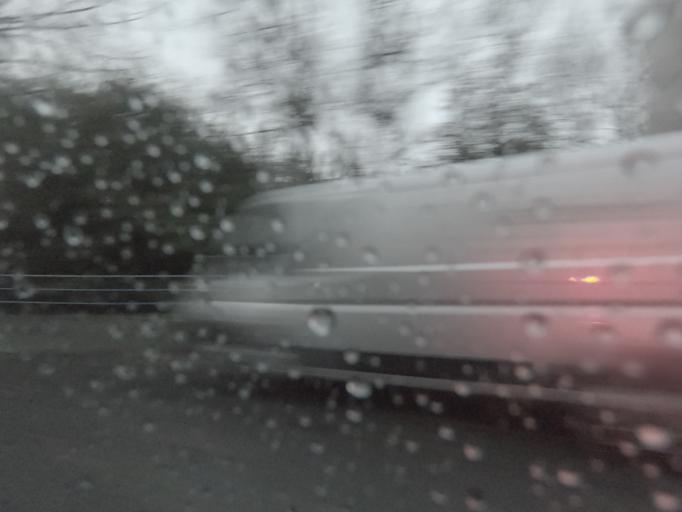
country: PT
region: Braga
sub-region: Braga
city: Braga
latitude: 41.5357
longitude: -8.4436
